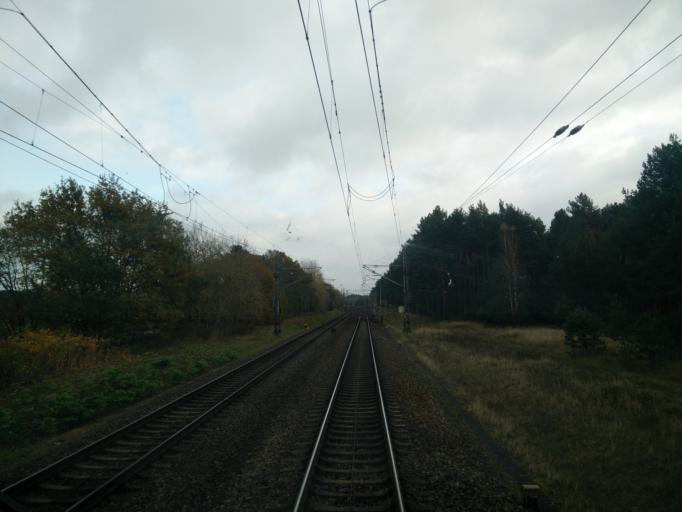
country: DE
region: Brandenburg
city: Plattenburg
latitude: 52.9101
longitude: 12.0656
